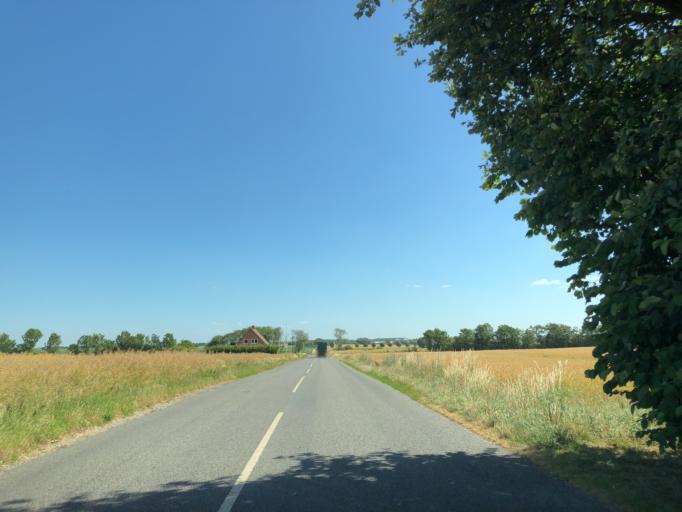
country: DK
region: North Denmark
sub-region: Vesthimmerland Kommune
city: Alestrup
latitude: 56.5819
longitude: 9.5900
